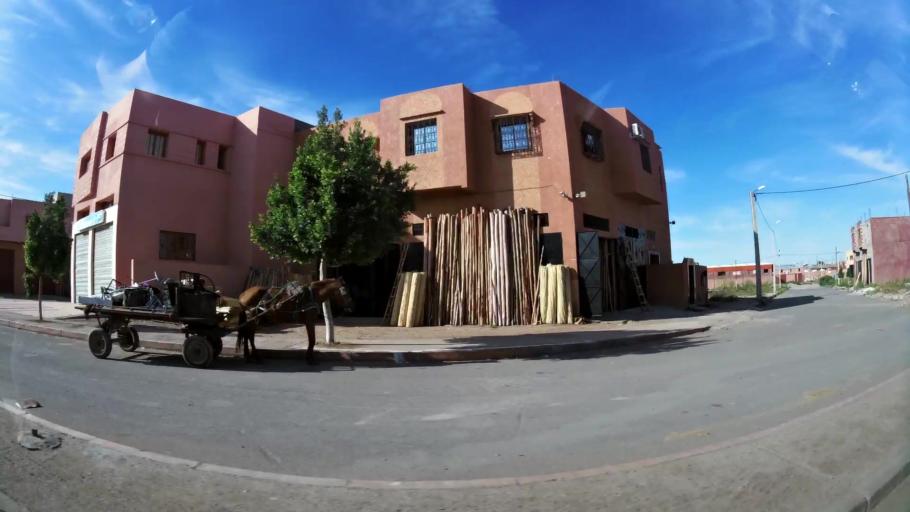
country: MA
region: Marrakech-Tensift-Al Haouz
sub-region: Marrakech
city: Marrakesh
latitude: 31.6826
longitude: -8.0591
